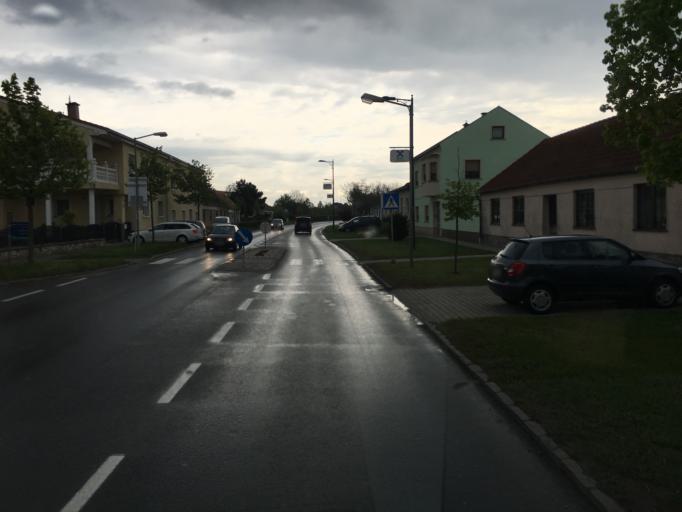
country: AT
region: Burgenland
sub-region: Politischer Bezirk Neusiedl am See
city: Parndorf
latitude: 47.9963
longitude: 16.8626
